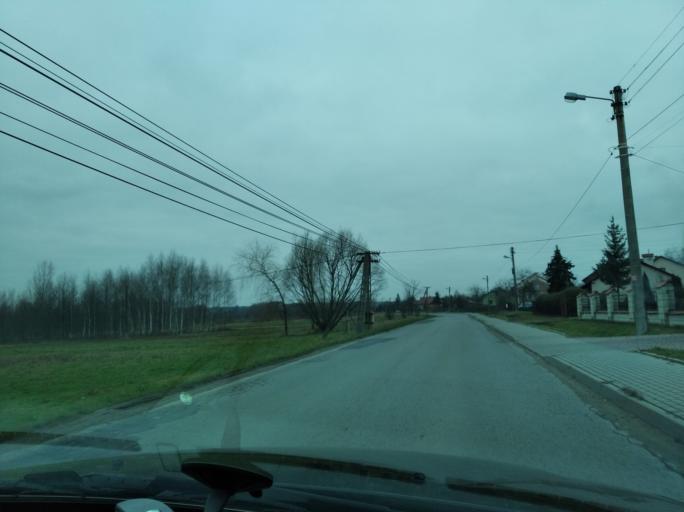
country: PL
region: Subcarpathian Voivodeship
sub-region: Powiat lancucki
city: Rakszawa
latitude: 50.1612
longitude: 22.2384
